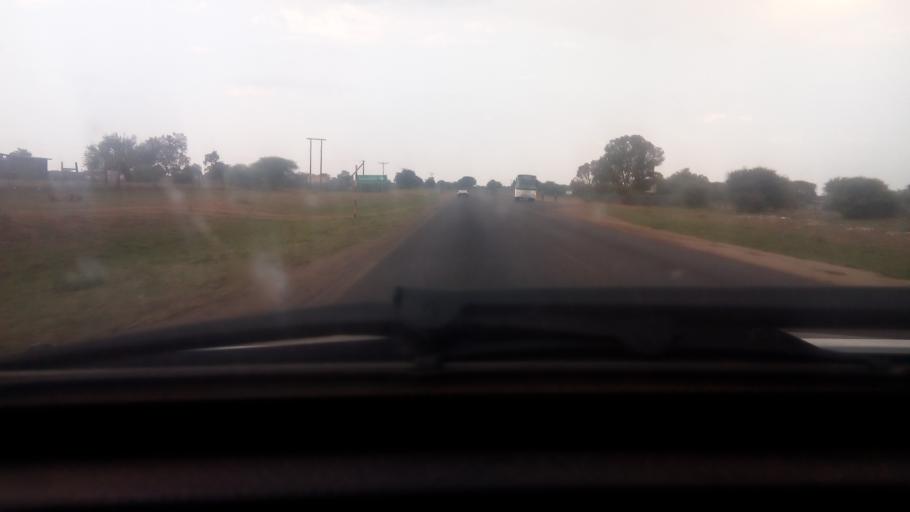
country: BW
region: Kweneng
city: Metsemotlhaba
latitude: -24.4773
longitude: 25.7236
